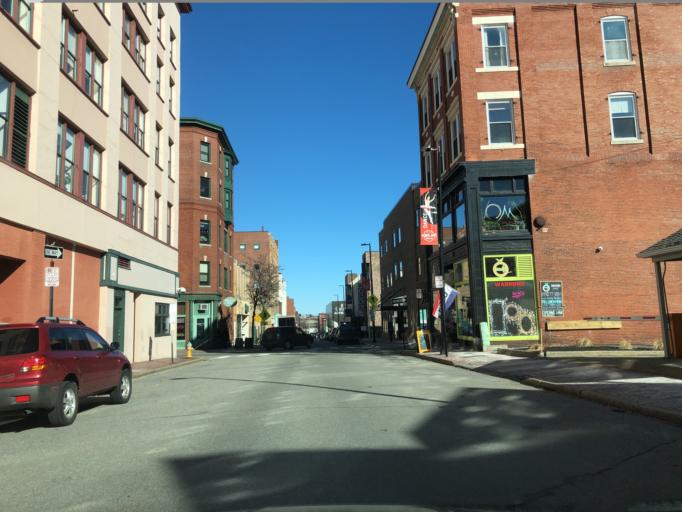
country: US
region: Maine
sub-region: Cumberland County
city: Portland
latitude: 43.6546
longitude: -70.2618
